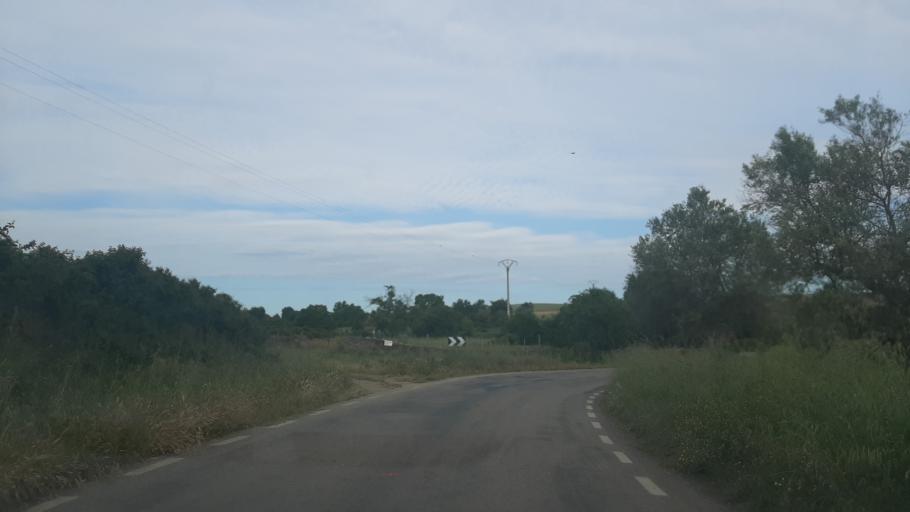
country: ES
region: Castille and Leon
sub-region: Provincia de Salamanca
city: Gallegos de Arganan
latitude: 40.6330
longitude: -6.7087
